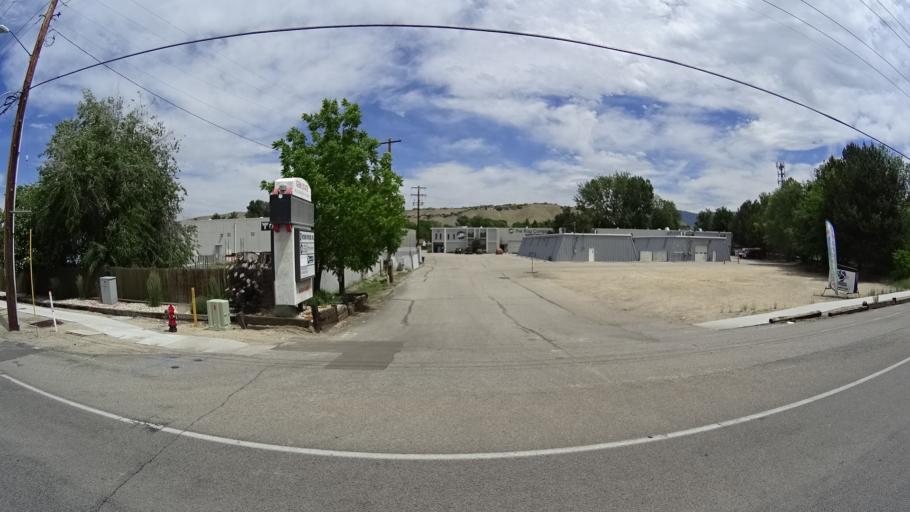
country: US
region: Idaho
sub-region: Ada County
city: Garden City
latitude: 43.6545
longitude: -116.2563
